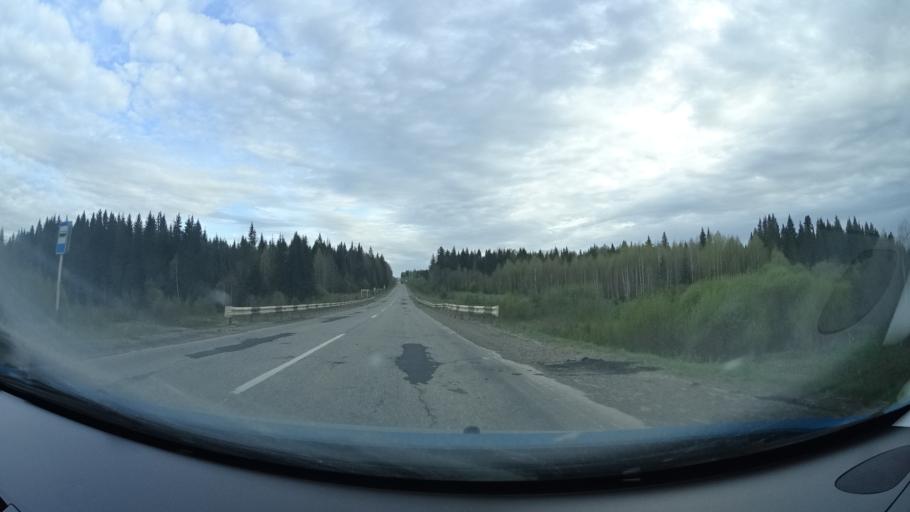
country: RU
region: Perm
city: Osa
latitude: 57.4214
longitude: 55.6225
